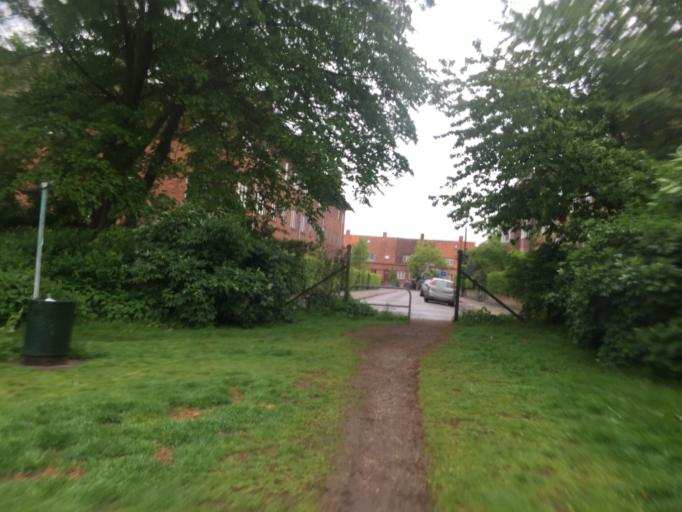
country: DK
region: Capital Region
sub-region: Frederiksberg Kommune
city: Frederiksberg
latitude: 55.6986
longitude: 12.5190
